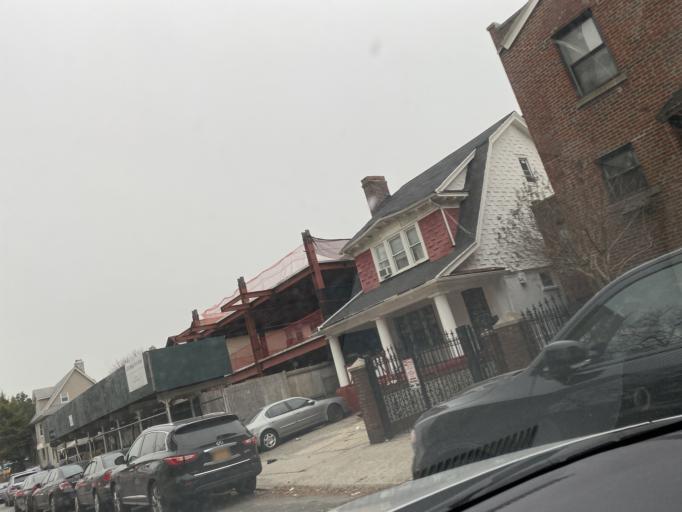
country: US
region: New York
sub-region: Kings County
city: Brooklyn
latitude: 40.6538
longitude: -73.9470
